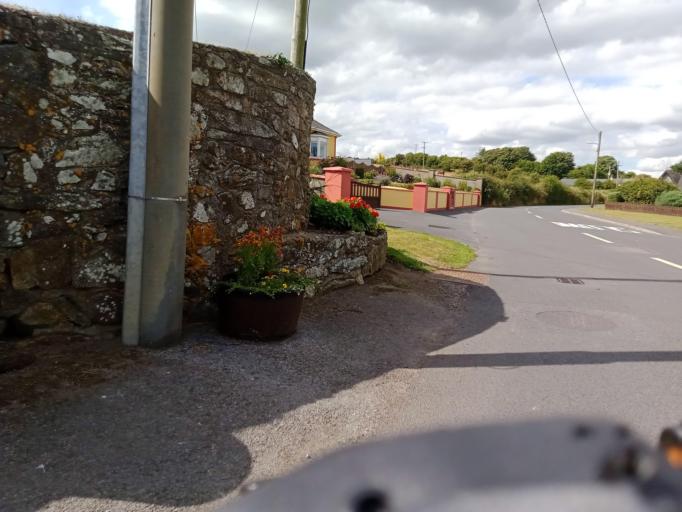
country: IE
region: Munster
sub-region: Waterford
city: Dungarvan
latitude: 52.1317
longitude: -7.4628
